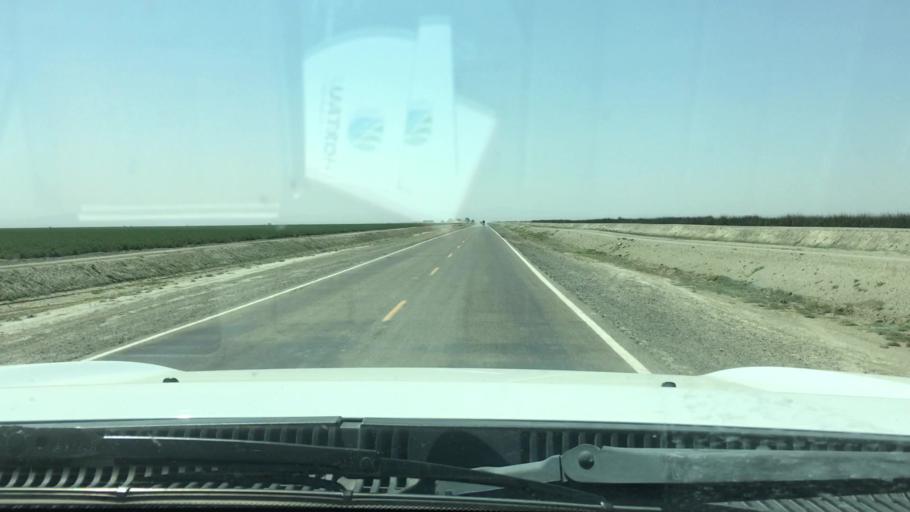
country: US
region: California
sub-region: Tulare County
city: Alpaugh
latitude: 35.9343
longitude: -119.6094
